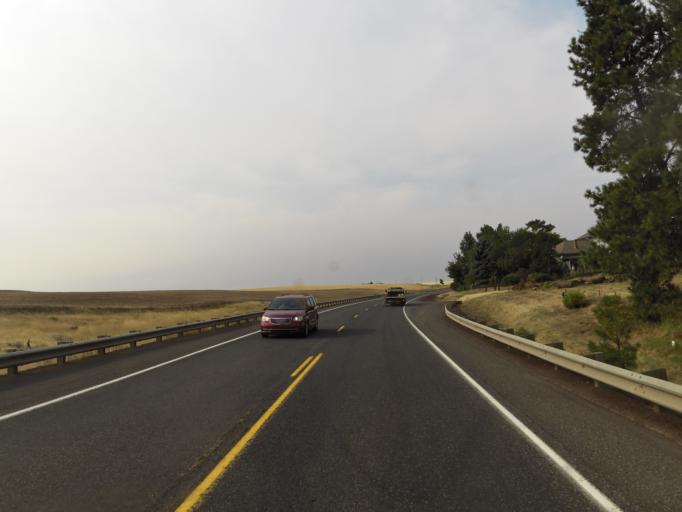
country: US
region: Oregon
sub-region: Sherman County
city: Moro
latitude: 45.4464
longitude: -120.7537
